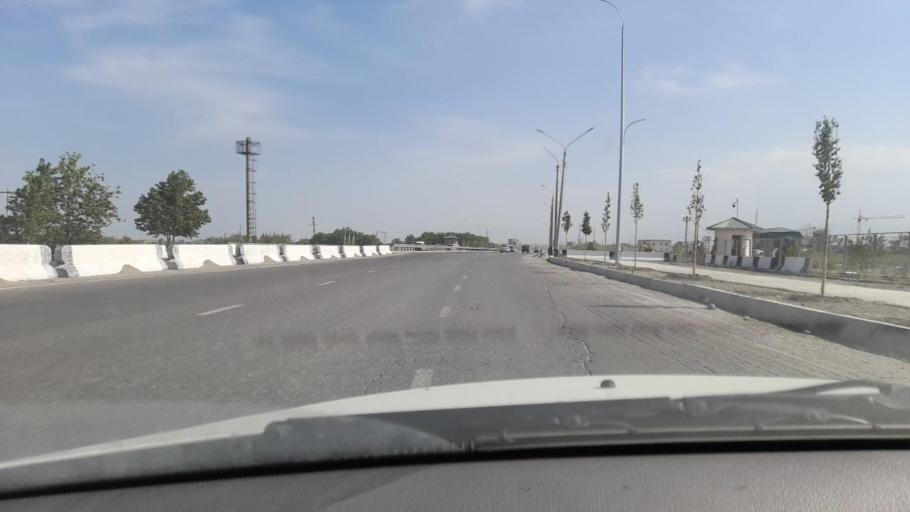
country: UZ
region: Samarqand
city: Daxbet
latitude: 39.7254
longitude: 66.9471
